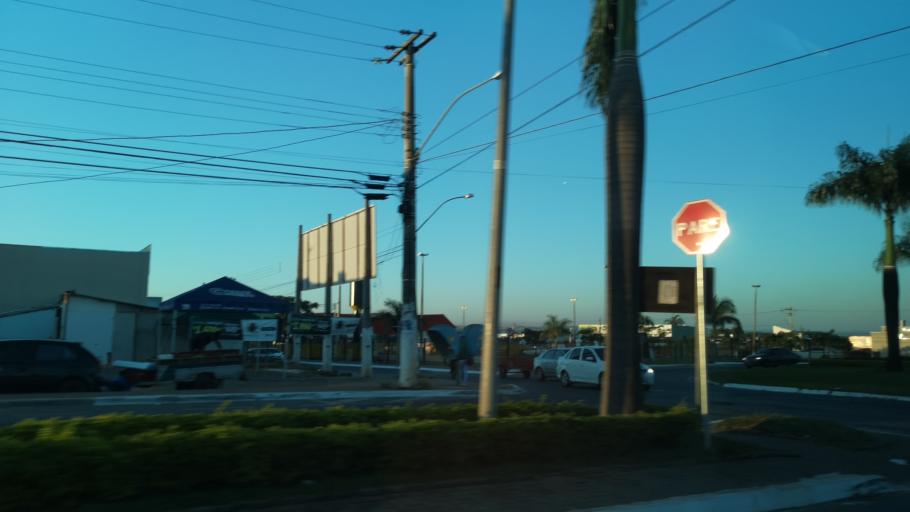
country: BR
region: Goias
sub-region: Senador Canedo
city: Senador Canedo
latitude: -16.6961
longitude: -49.1025
